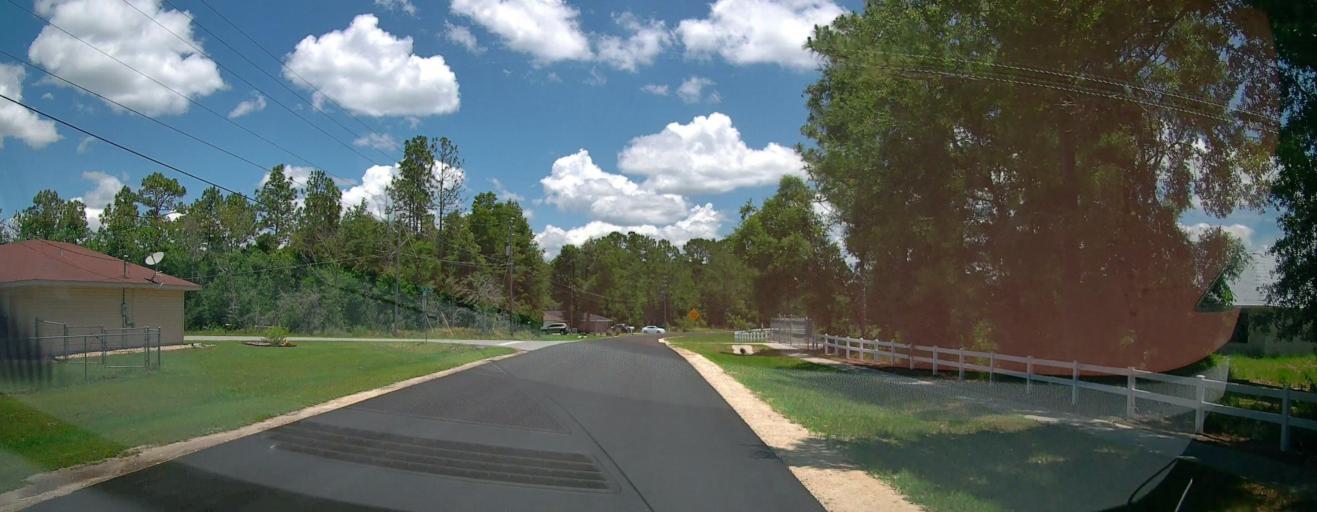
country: US
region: Florida
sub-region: Marion County
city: Silver Springs Shores
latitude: 29.1366
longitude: -82.0215
